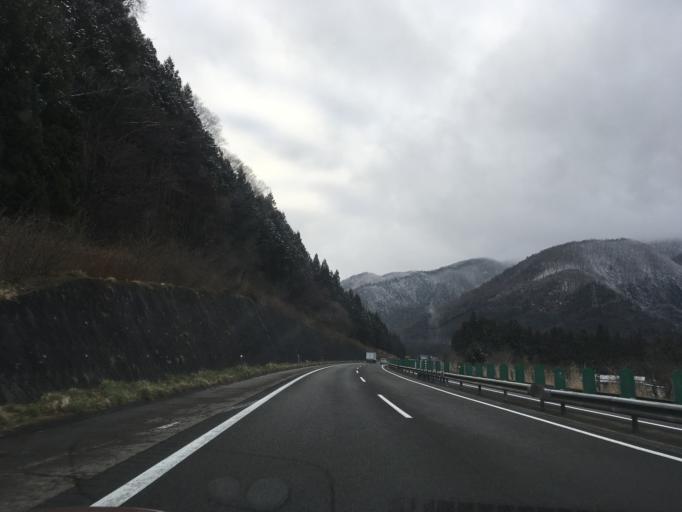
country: JP
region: Miyagi
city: Shiroishi
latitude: 38.2006
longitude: 140.5825
